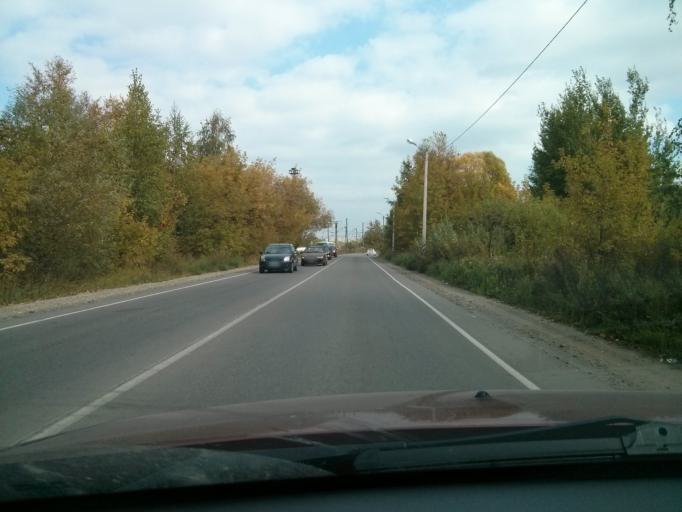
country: RU
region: Vladimir
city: Murom
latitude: 55.5616
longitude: 42.0285
